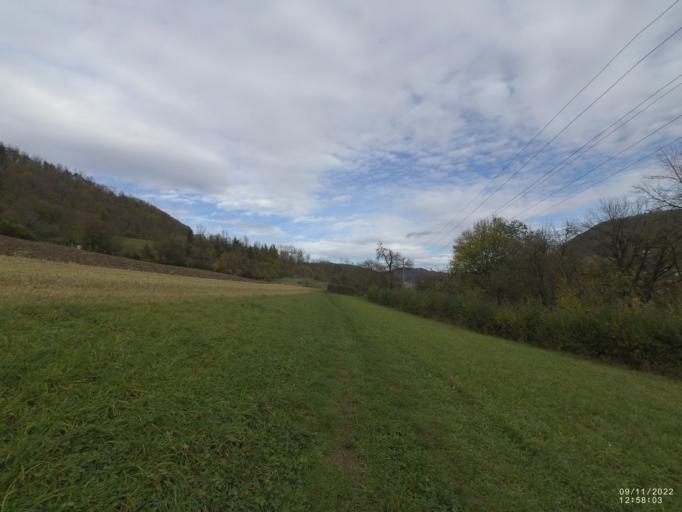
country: DE
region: Baden-Wuerttemberg
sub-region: Regierungsbezirk Stuttgart
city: Bad Uberkingen
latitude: 48.6137
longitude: 9.8057
